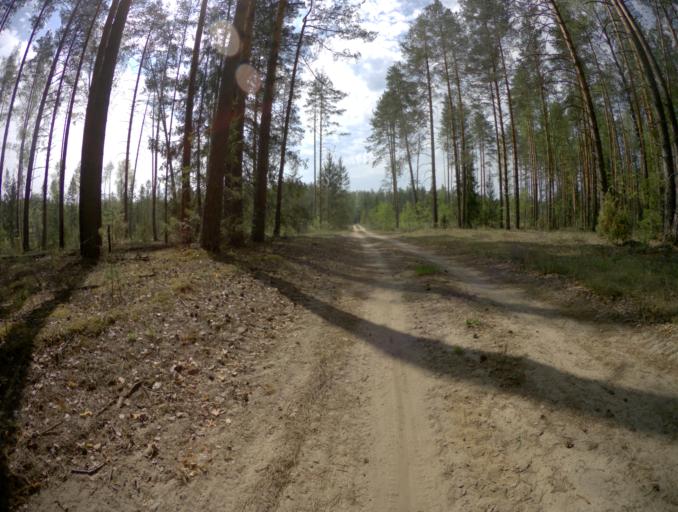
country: RU
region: Ivanovo
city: Yuzha
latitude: 56.4807
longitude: 42.1310
